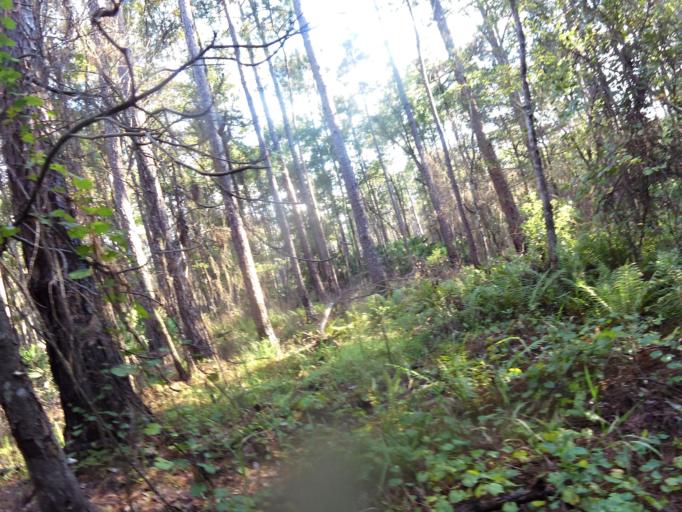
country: US
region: Florida
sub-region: Clay County
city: Orange Park
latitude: 30.2439
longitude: -81.6987
